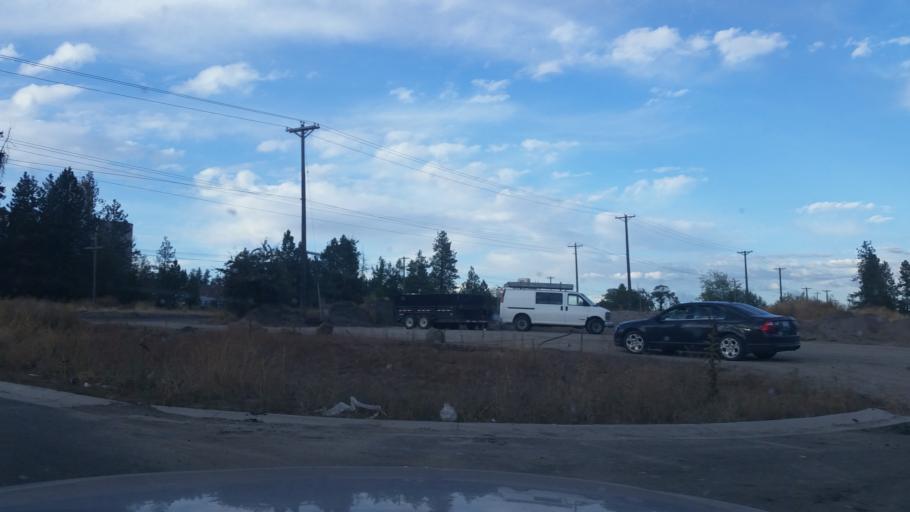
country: US
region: Washington
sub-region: Spokane County
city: Cheney
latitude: 47.4826
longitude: -117.5762
